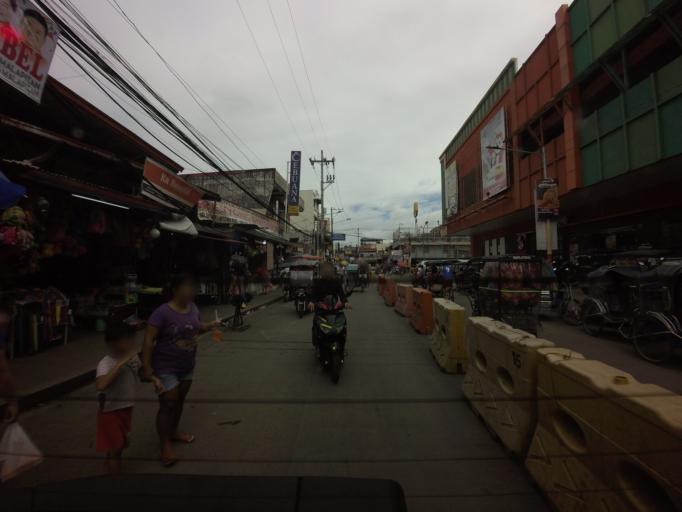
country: PH
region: Metro Manila
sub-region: Caloocan City
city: Niugan
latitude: 14.6380
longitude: 120.9747
